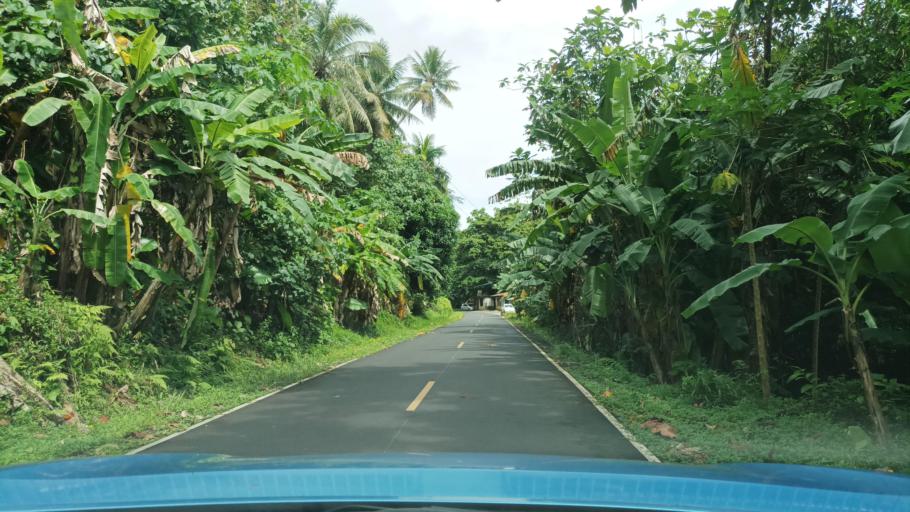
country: FM
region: Pohnpei
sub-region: Madolenihm Municipality
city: Madolenihm Municipality Government
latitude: 6.8757
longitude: 158.3338
